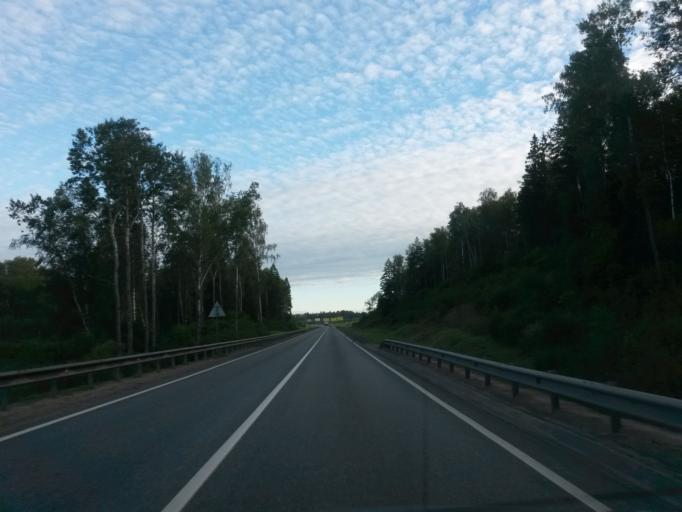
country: RU
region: Vladimir
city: Strunino
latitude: 56.5534
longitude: 38.5884
